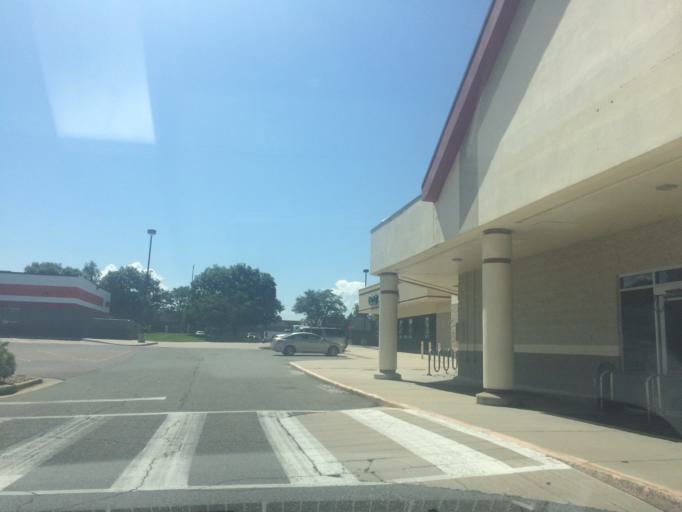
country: US
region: Colorado
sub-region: Broomfield County
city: Broomfield
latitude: 39.9151
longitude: -105.0706
